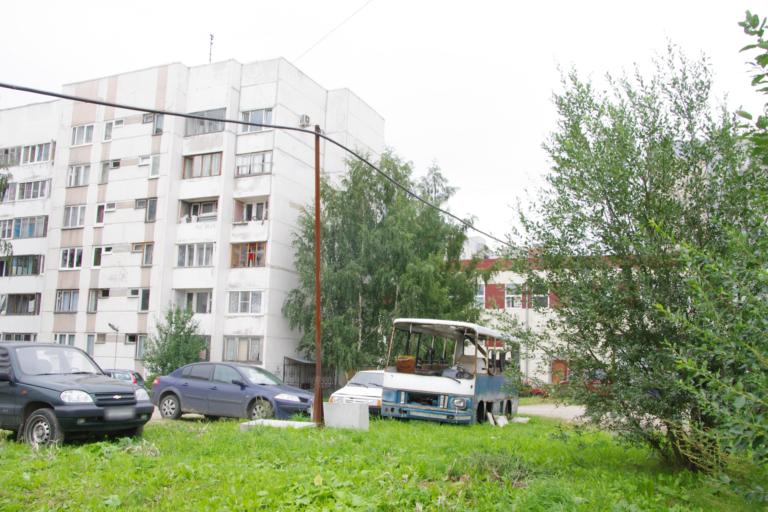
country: RU
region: Leningrad
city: Untolovo
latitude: 59.9853
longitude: 30.2058
